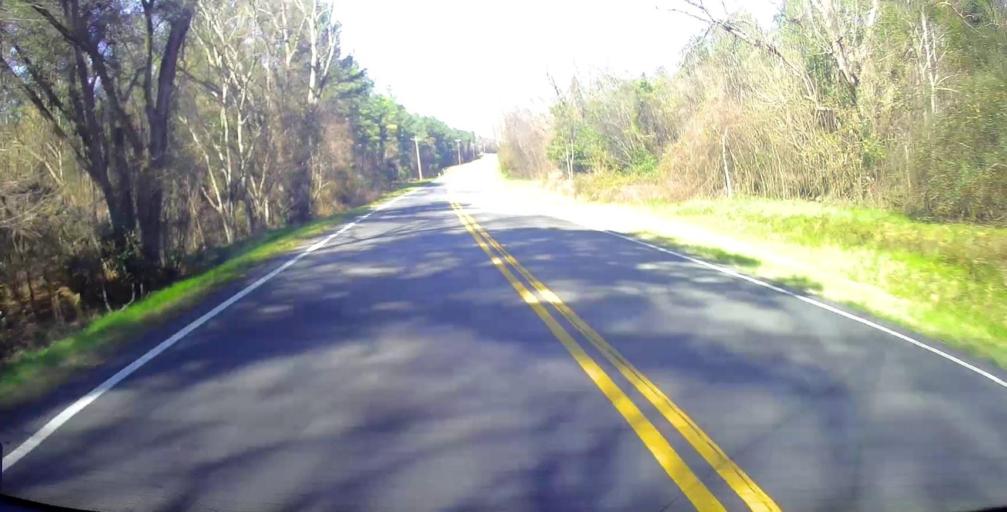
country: US
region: Georgia
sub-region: Macon County
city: Montezuma
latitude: 32.3497
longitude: -84.0188
